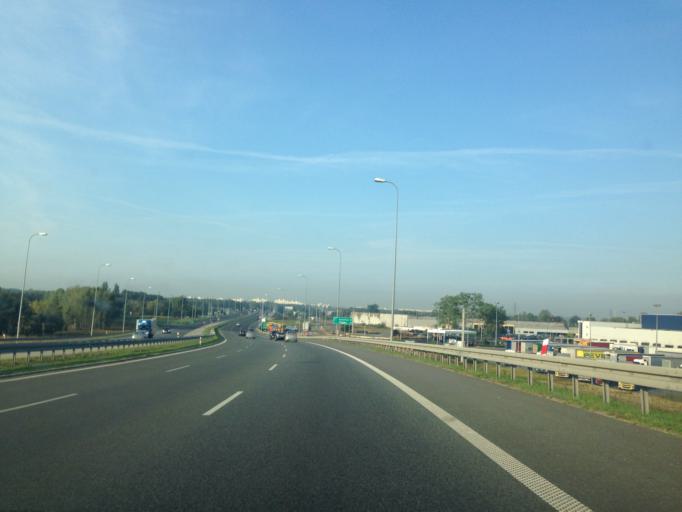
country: PL
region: Kujawsko-Pomorskie
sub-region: Powiat torunski
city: Lubicz Dolny
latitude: 53.0382
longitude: 18.7301
